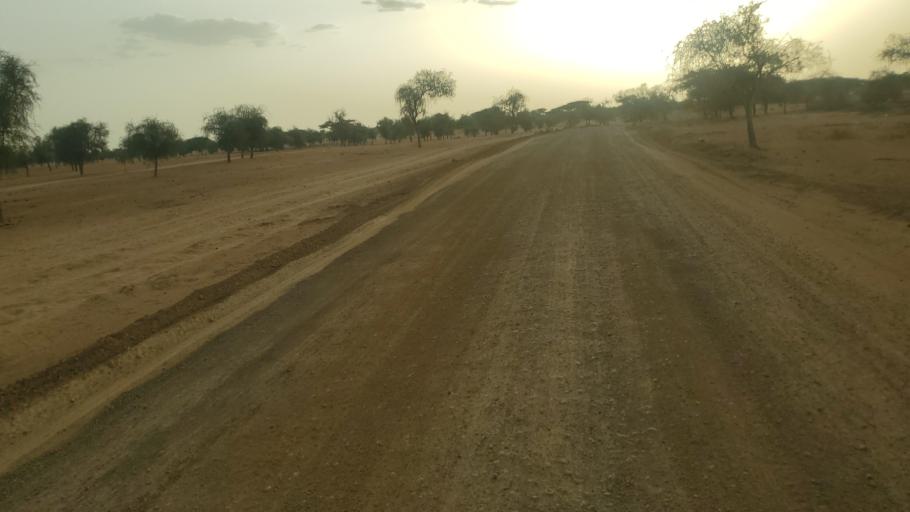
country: SN
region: Louga
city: Dara
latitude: 15.3700
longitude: -15.5772
